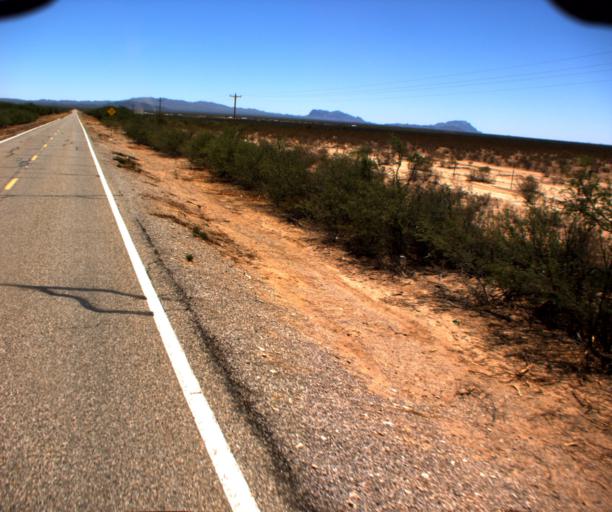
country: US
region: Arizona
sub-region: Pima County
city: Ajo
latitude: 32.1869
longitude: -112.3838
